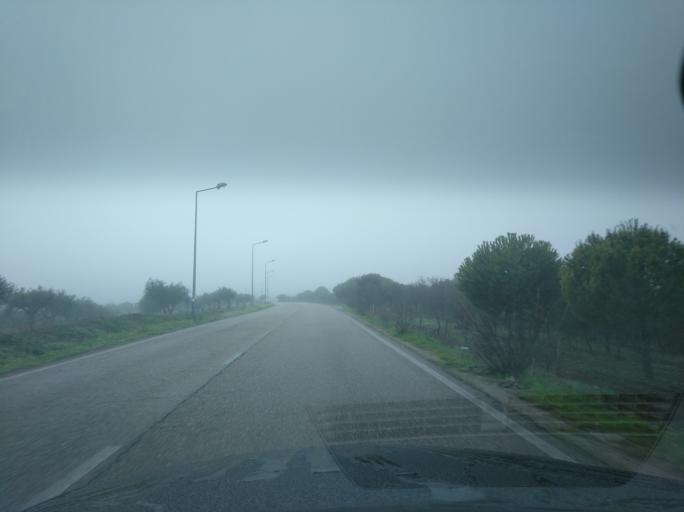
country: PT
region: Portalegre
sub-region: Campo Maior
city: Campo Maior
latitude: 39.0246
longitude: -7.0738
